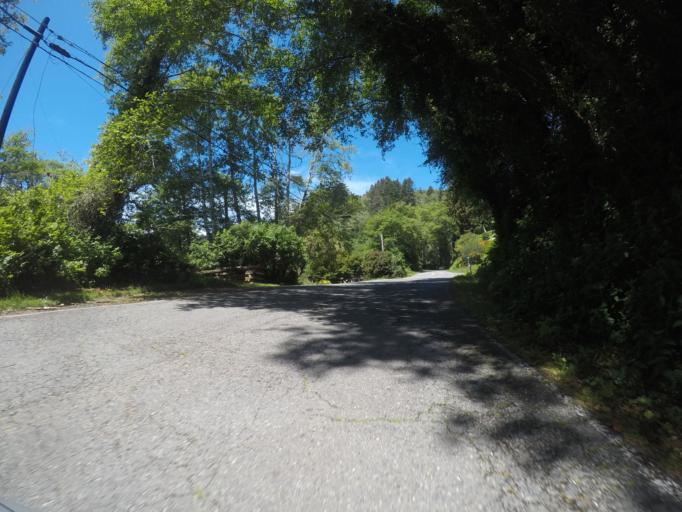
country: US
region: California
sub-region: Del Norte County
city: Bertsch-Oceanview
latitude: 41.5473
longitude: -124.0707
